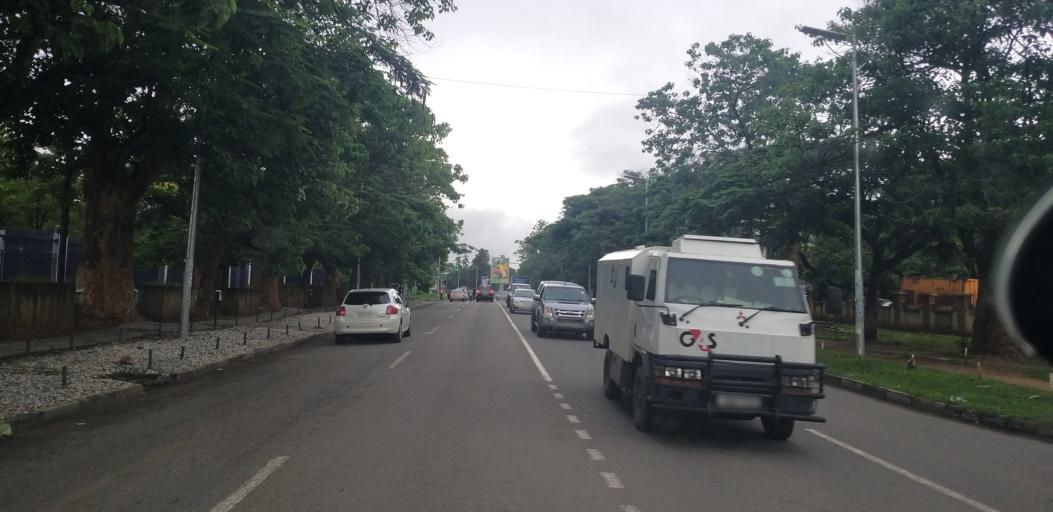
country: ZM
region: Lusaka
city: Lusaka
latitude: -15.4240
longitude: 28.3107
